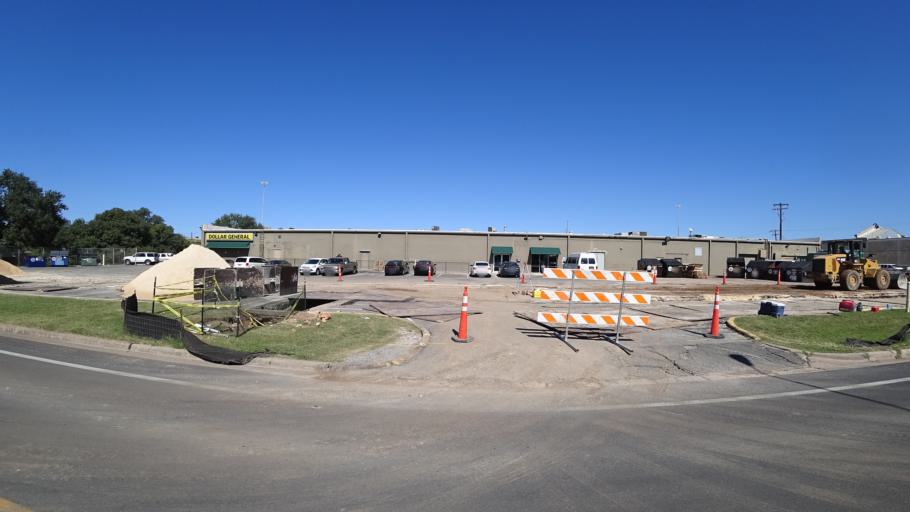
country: US
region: Texas
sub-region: Travis County
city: Rollingwood
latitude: 30.2293
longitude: -97.7916
